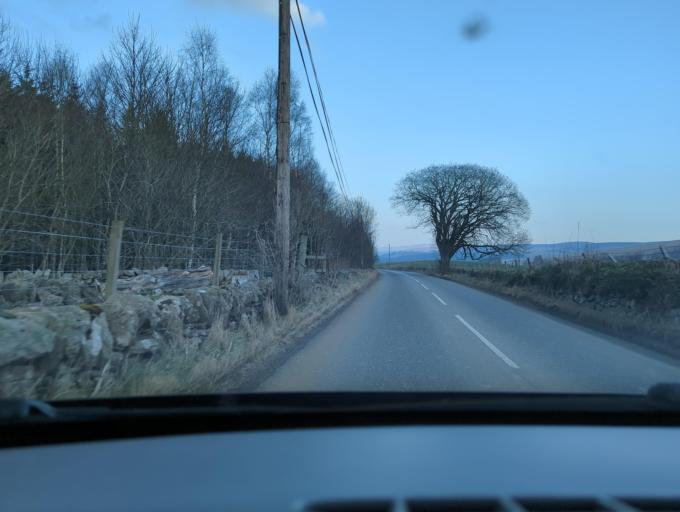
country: GB
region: Scotland
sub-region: Perth and Kinross
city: Aberfeldy
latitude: 56.5314
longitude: -3.7145
